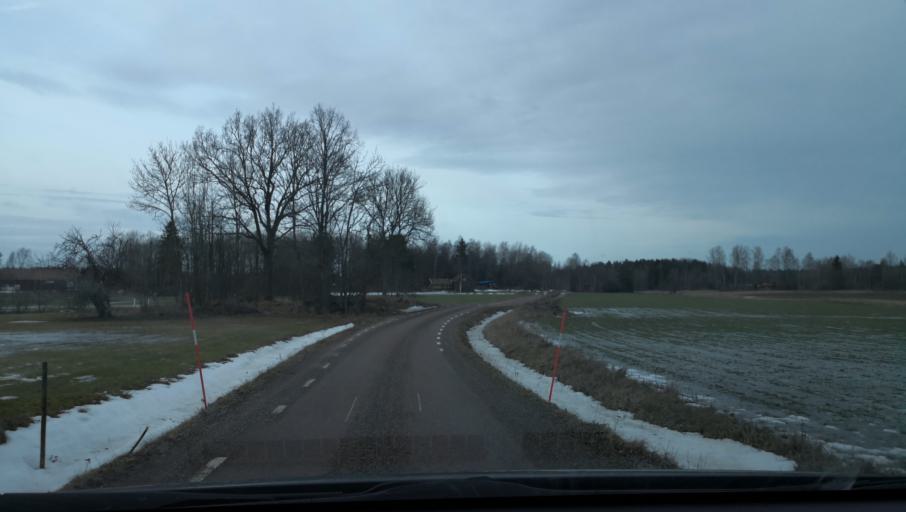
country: SE
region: Vaestmanland
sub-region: Vasteras
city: Skultuna
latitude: 59.6221
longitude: 16.4133
